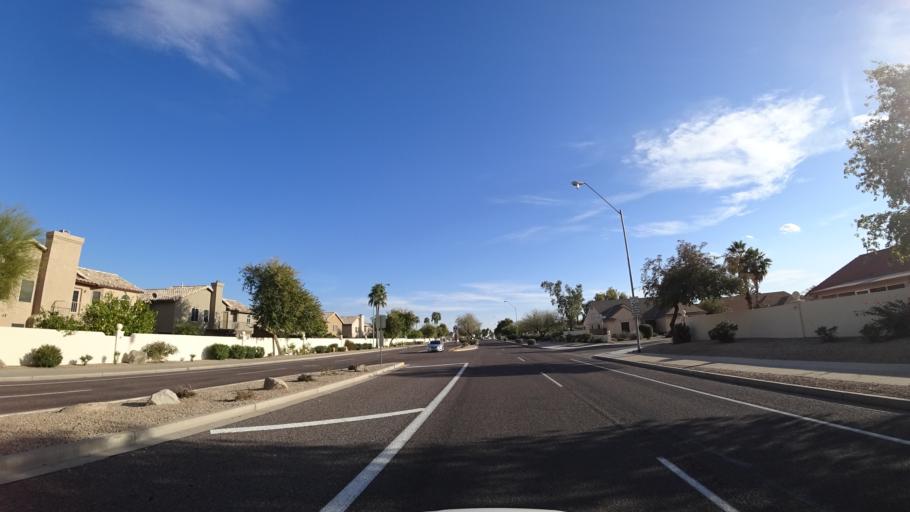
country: US
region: Arizona
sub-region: Maricopa County
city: Sun City
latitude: 33.6194
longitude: -112.2549
